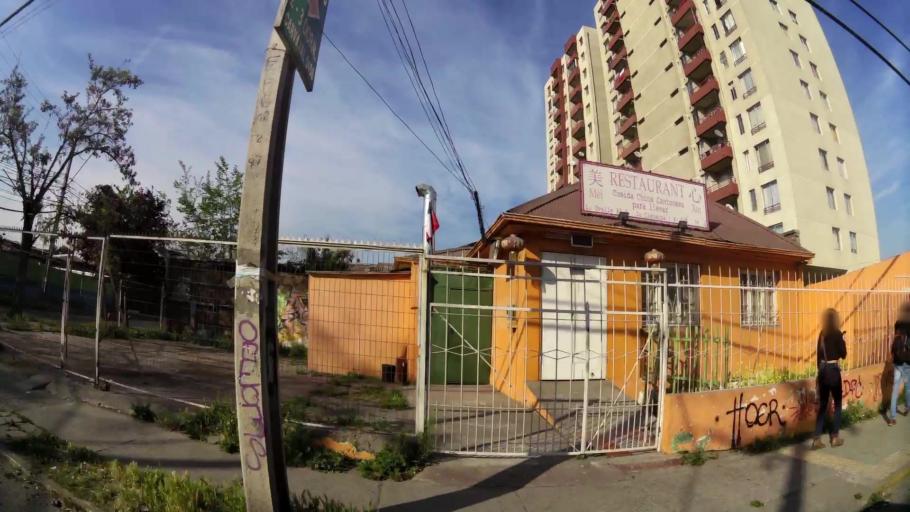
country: CL
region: Santiago Metropolitan
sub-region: Provincia de Santiago
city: Santiago
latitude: -33.5135
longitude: -70.6624
